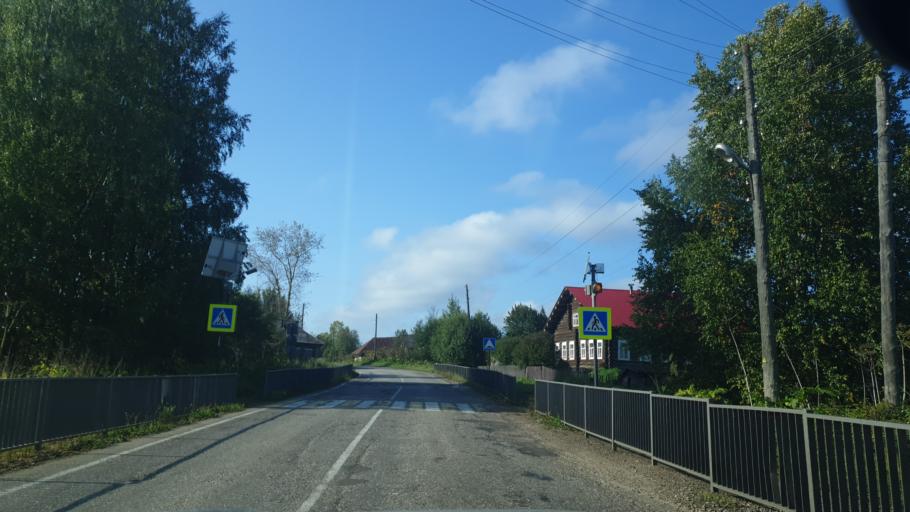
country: RU
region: Komi Republic
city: Vizinga
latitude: 60.9394
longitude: 50.2324
